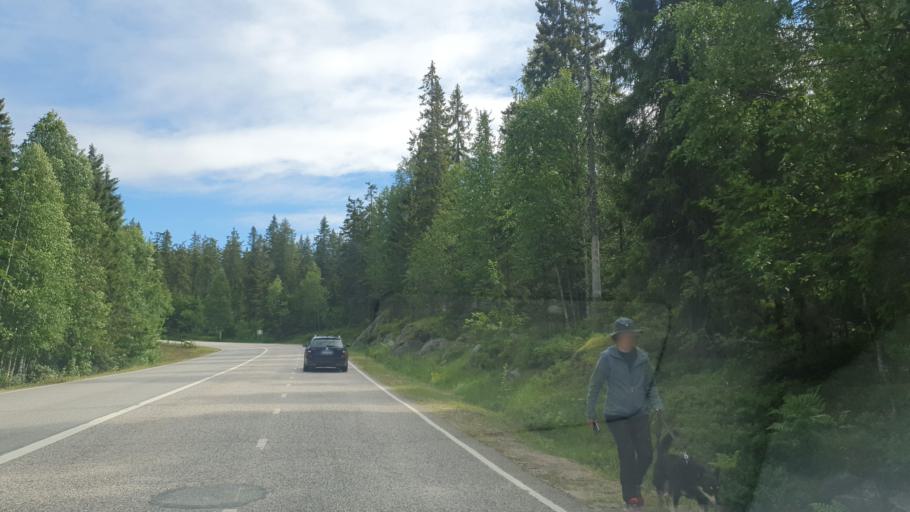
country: FI
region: Kainuu
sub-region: Kajaani
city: Vuokatti
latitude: 64.1290
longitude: 28.2564
